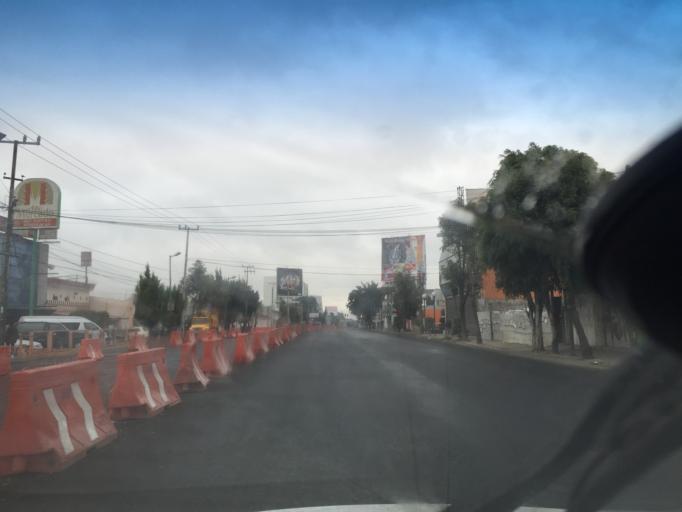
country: MX
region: Mexico
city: Colonia Lindavista
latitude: 19.4922
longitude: -99.1402
